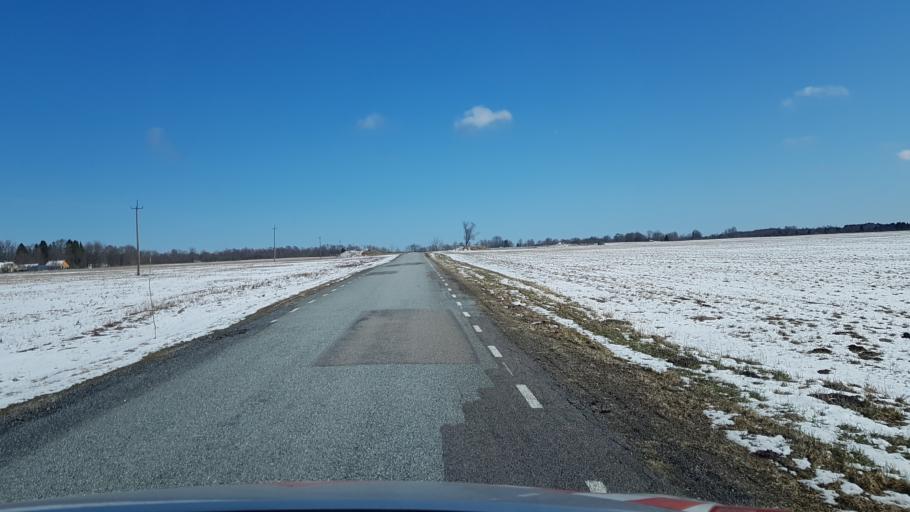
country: EE
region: Laeaene-Virumaa
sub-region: Kadrina vald
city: Kadrina
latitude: 59.5302
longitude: 26.0254
